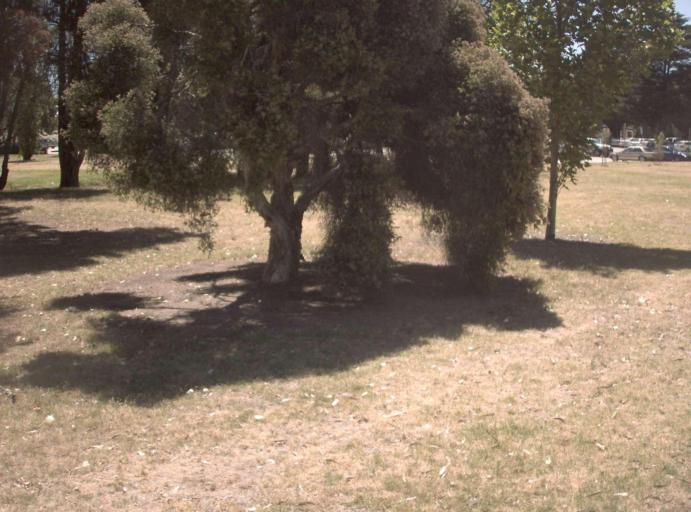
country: AU
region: Victoria
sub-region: Port Phillip
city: St Kilda West
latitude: -37.8490
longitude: 144.9777
